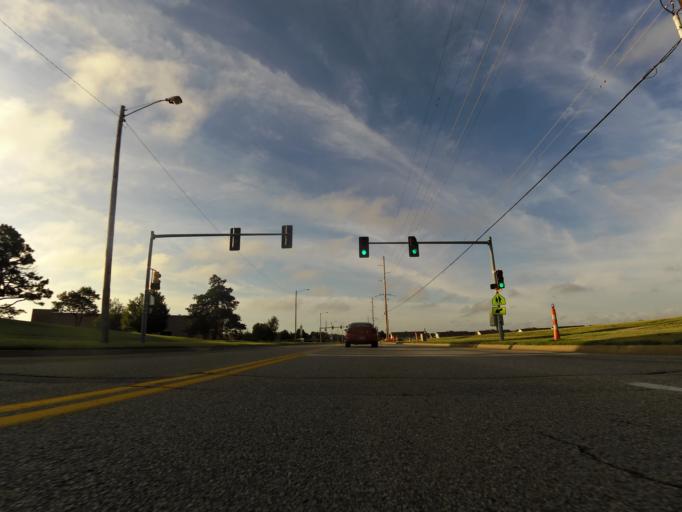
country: US
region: Kansas
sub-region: Sedgwick County
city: Bellaire
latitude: 37.7344
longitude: -97.2624
